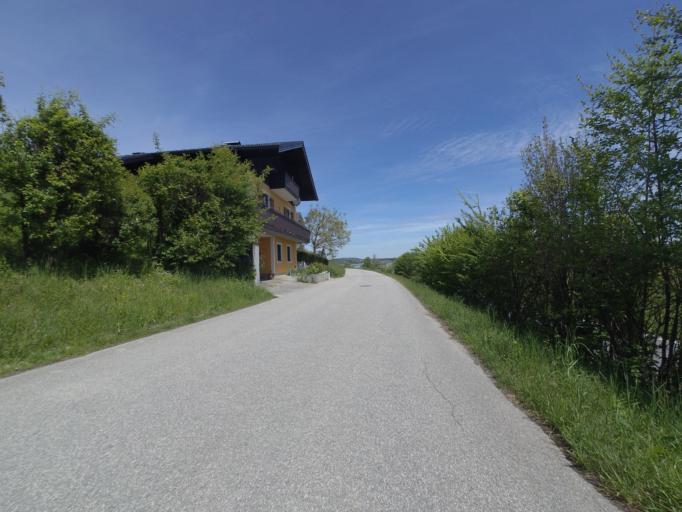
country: AT
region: Salzburg
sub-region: Politischer Bezirk Salzburg-Umgebung
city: Seeham
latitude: 47.9797
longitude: 13.0808
